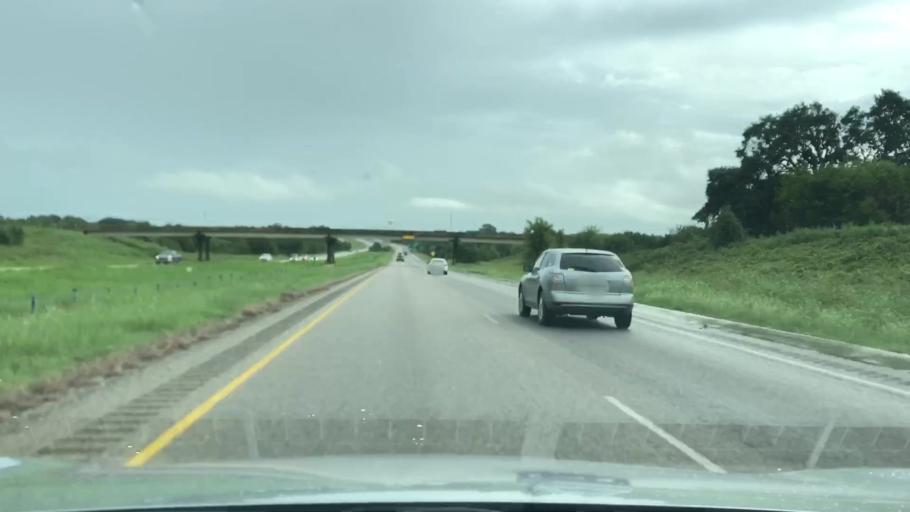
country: US
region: Texas
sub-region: Fayette County
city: Schulenburg
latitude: 29.6901
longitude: -96.9301
